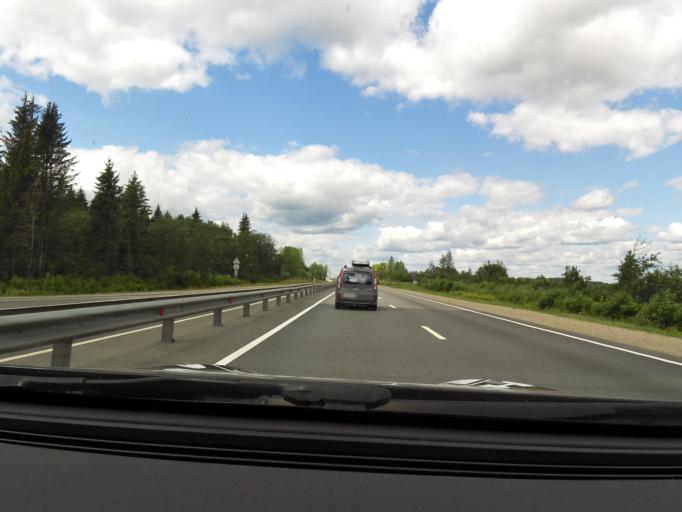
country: RU
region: Tverskaya
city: Torzhok
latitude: 57.0205
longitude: 35.0488
